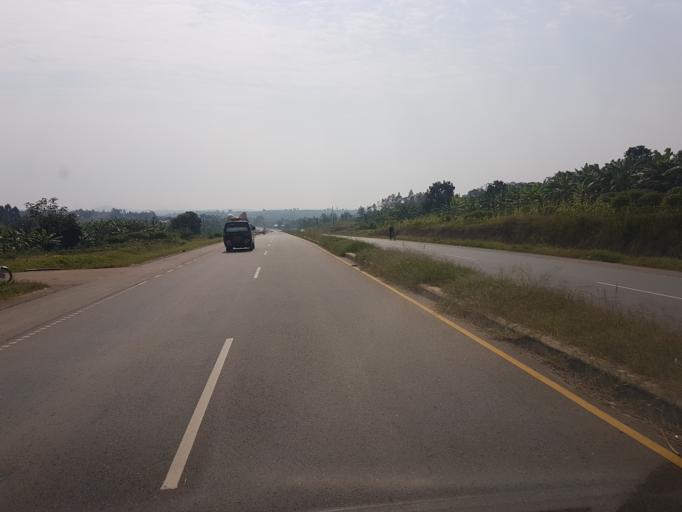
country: UG
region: Western Region
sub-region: Mbarara District
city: Bwizibwera
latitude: -0.6405
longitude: 30.5905
